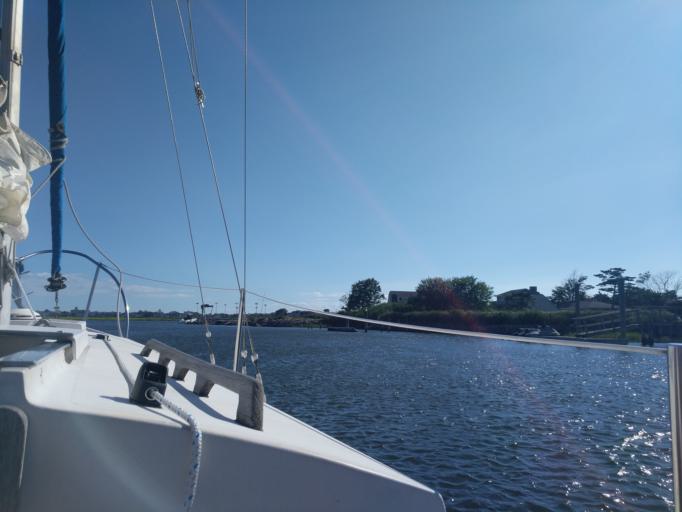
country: US
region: New York
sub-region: Nassau County
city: Barnum Island
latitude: 40.6057
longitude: -73.6421
